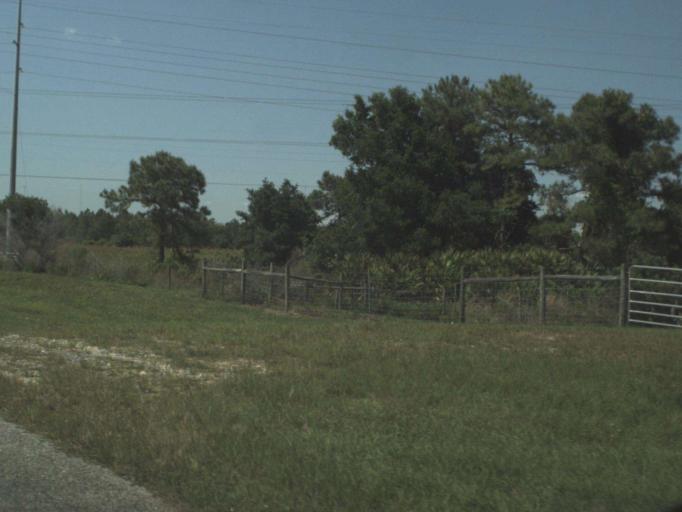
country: US
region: Florida
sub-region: Orange County
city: Wedgefield
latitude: 28.5023
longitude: -81.0515
